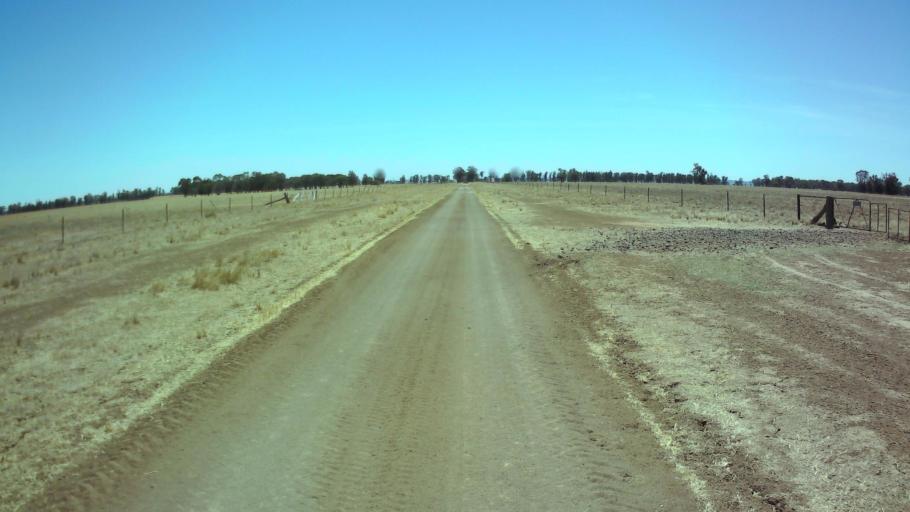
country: AU
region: New South Wales
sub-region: Weddin
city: Grenfell
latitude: -33.9810
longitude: 147.7361
